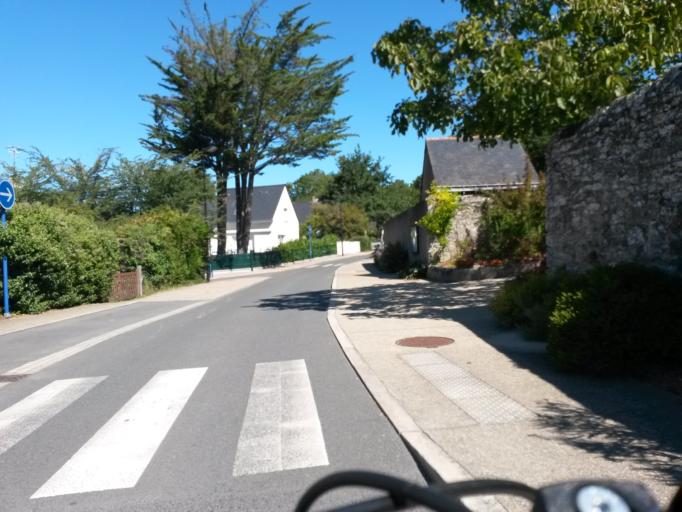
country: FR
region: Pays de la Loire
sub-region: Departement de la Loire-Atlantique
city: Mesquer
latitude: 47.4007
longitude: -2.4610
